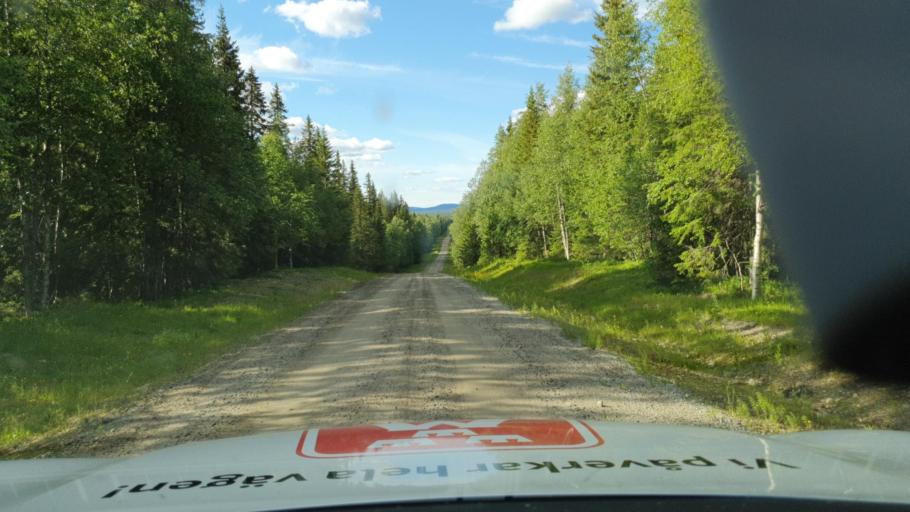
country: SE
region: Vaesterbotten
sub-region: Lycksele Kommun
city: Lycksele
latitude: 64.4270
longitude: 18.2769
